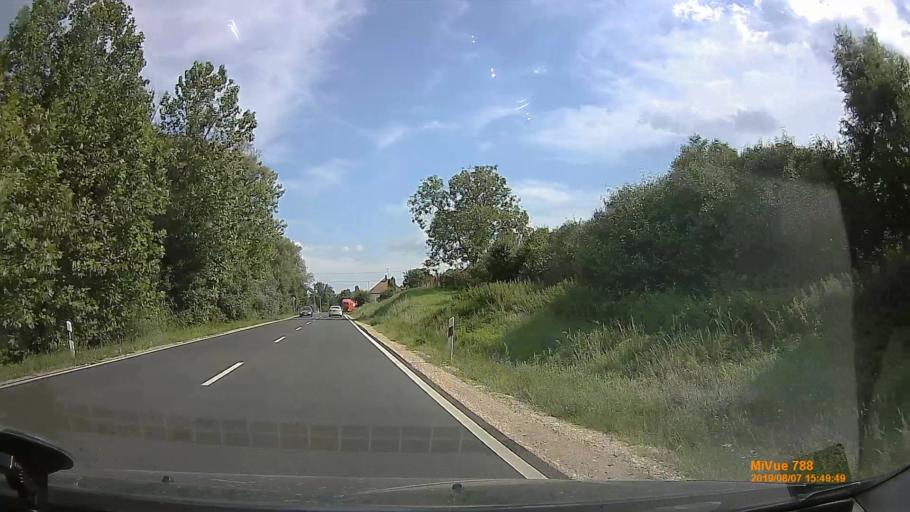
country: HU
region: Vas
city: Jak
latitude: 47.1460
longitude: 16.6453
